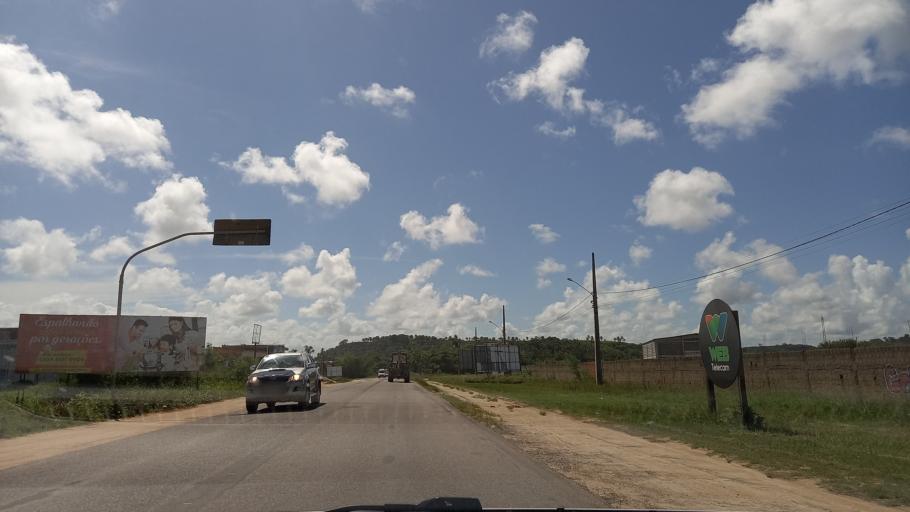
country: BR
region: Pernambuco
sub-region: Sao Jose Da Coroa Grande
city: Sao Jose da Coroa Grande
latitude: -8.8867
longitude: -35.1534
